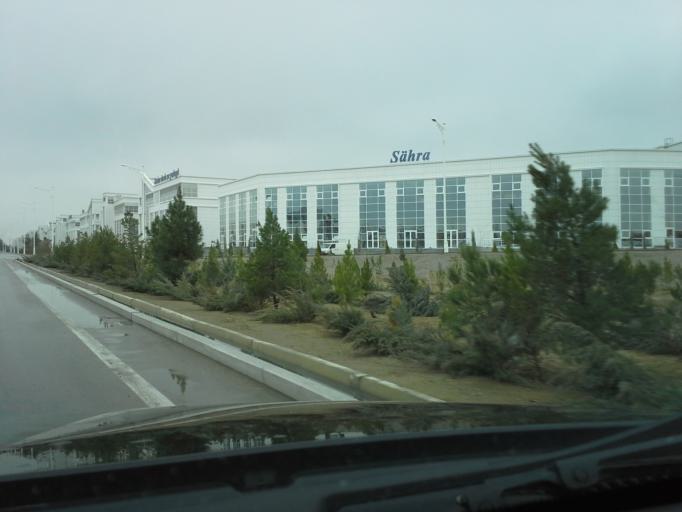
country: TM
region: Ahal
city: Ashgabat
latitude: 37.9512
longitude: 58.4351
